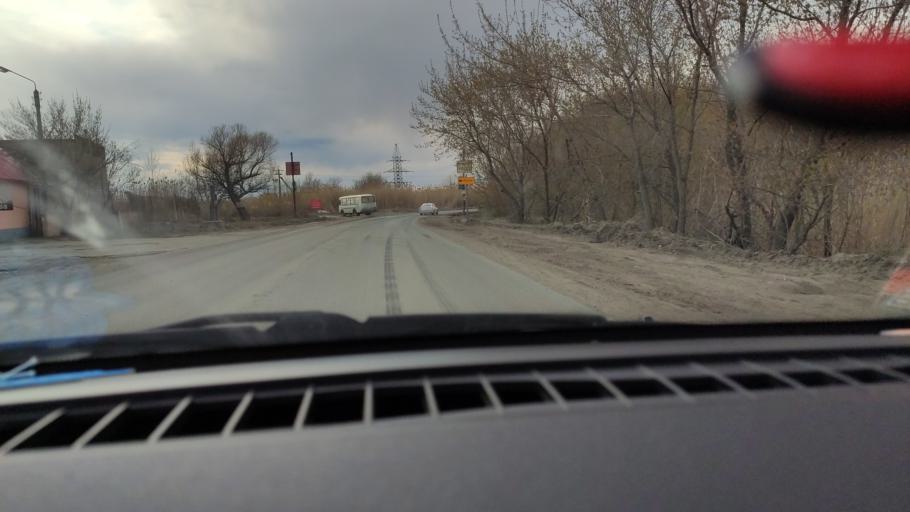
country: RU
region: Saratov
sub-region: Saratovskiy Rayon
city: Saratov
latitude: 51.6171
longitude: 45.9488
